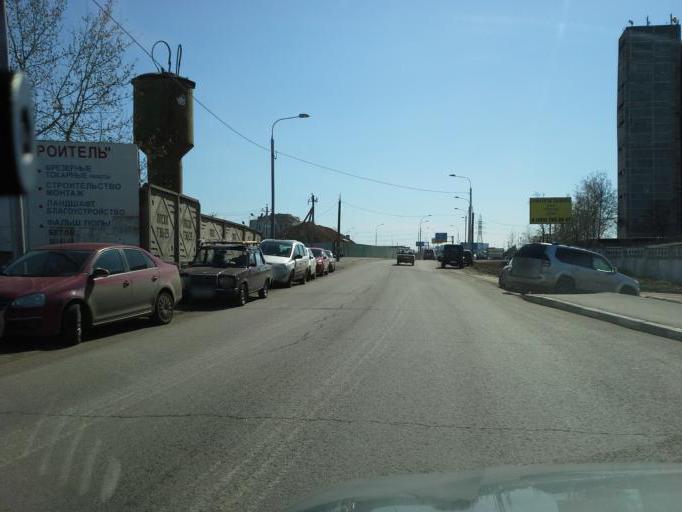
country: RU
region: Moskovskaya
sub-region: Leninskiy Rayon
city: Vnukovo
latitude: 55.6241
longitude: 37.2653
